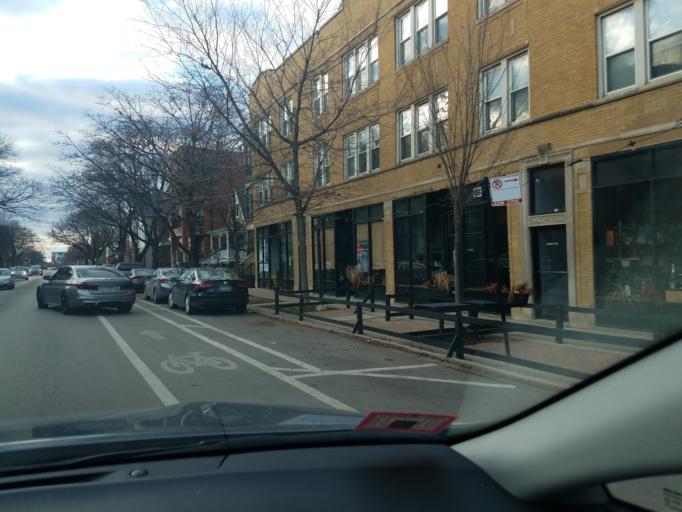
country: US
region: Illinois
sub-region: Cook County
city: Lincolnwood
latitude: 41.9432
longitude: -87.6847
